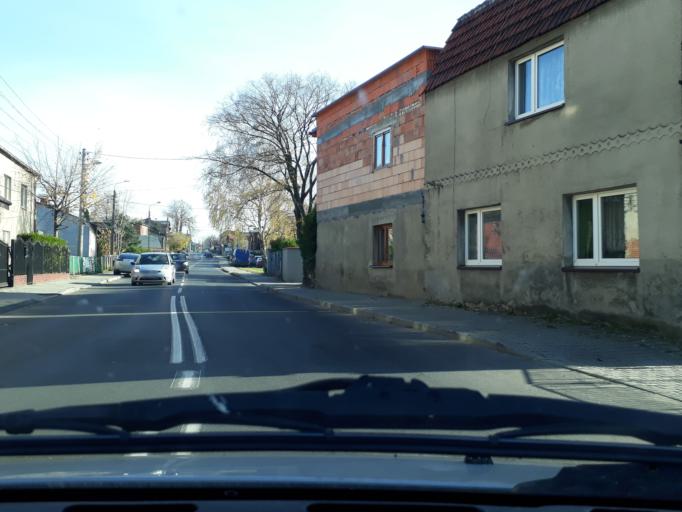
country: PL
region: Silesian Voivodeship
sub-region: Powiat tarnogorski
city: Tarnowskie Gory
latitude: 50.4226
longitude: 18.8719
